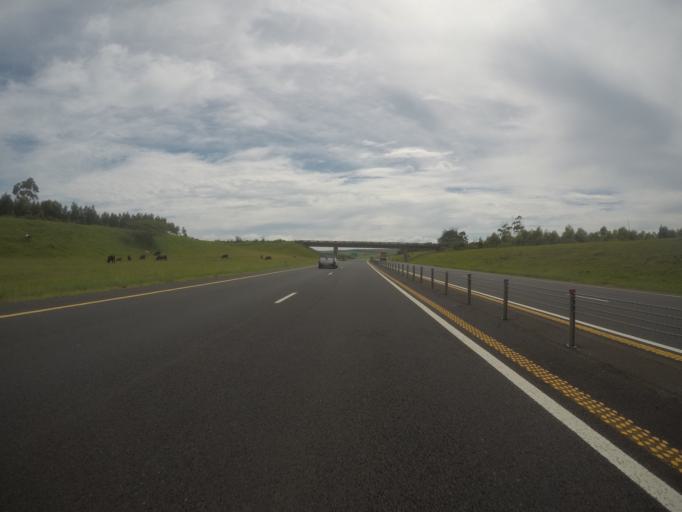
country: ZA
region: KwaZulu-Natal
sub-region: iLembe District Municipality
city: Mandeni
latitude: -29.0588
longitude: 31.6282
